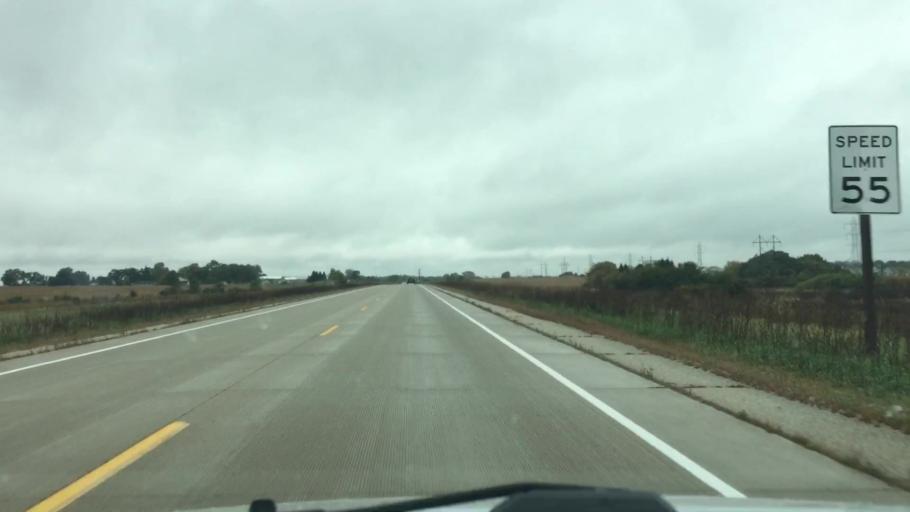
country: US
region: Wisconsin
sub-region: Walworth County
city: Whitewater
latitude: 42.8193
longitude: -88.7120
